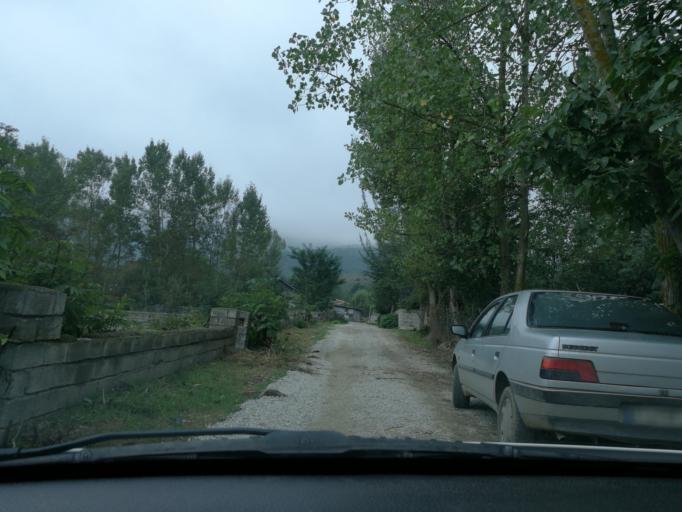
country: IR
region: Mazandaran
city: `Abbasabad
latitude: 36.4996
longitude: 51.2092
